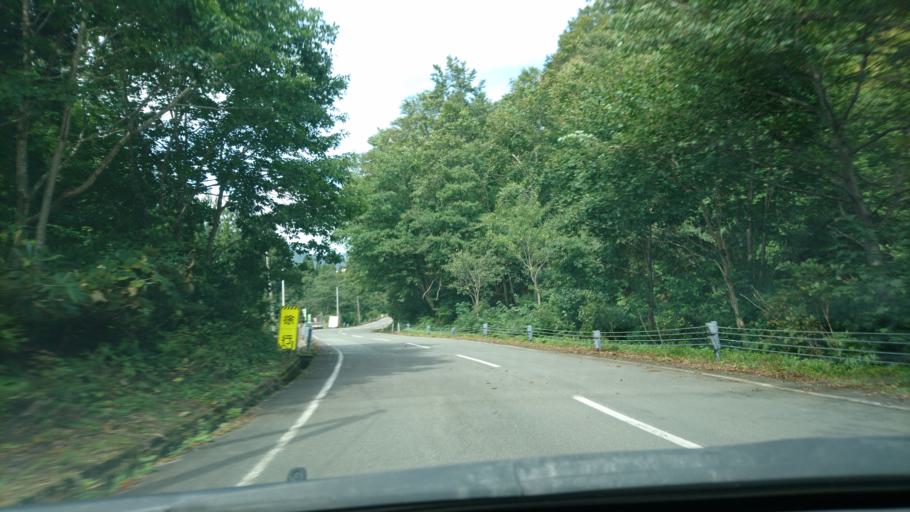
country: JP
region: Akita
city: Yuzawa
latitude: 39.0260
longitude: 140.7282
